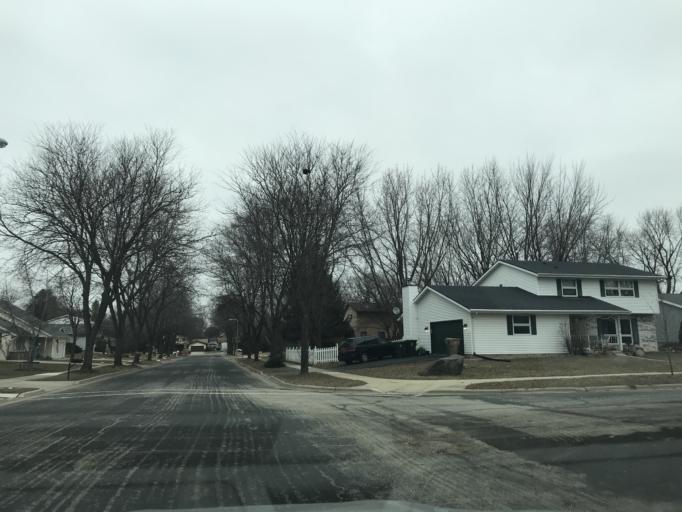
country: US
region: Wisconsin
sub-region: Dane County
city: Monona
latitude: 43.0971
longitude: -89.2958
